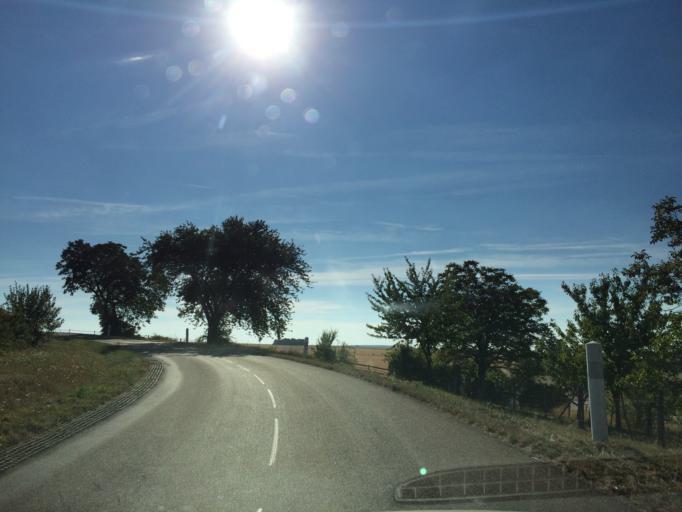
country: FR
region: Bourgogne
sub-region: Departement de l'Yonne
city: Cheny
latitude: 47.9308
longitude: 3.5067
